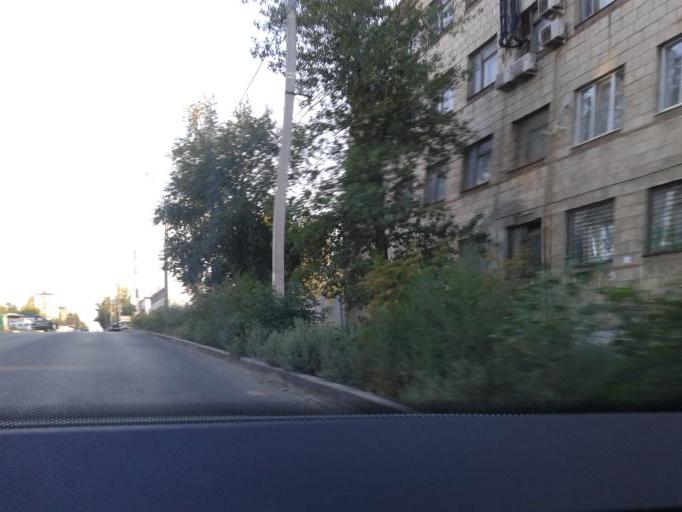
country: RU
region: Volgograd
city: Gorodishche
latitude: 48.7711
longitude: 44.4776
